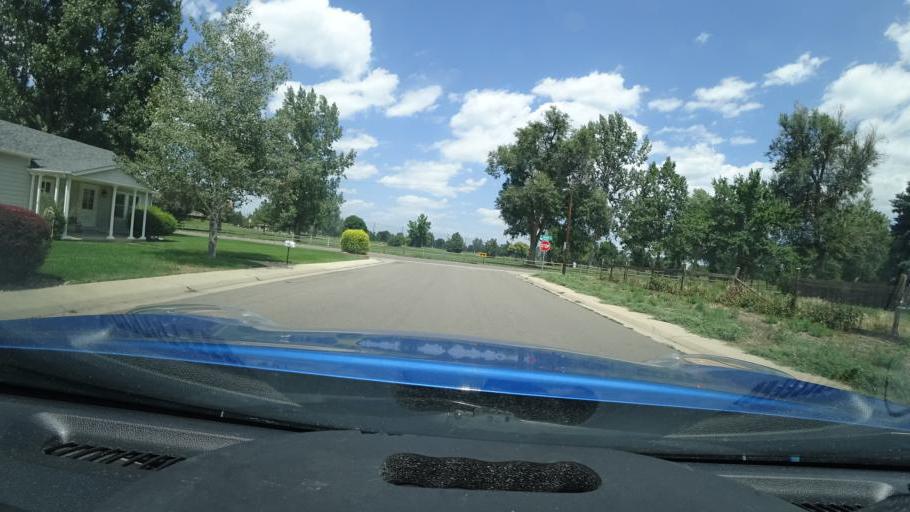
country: US
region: Colorado
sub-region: Arapahoe County
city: Englewood
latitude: 39.6817
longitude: -104.9960
